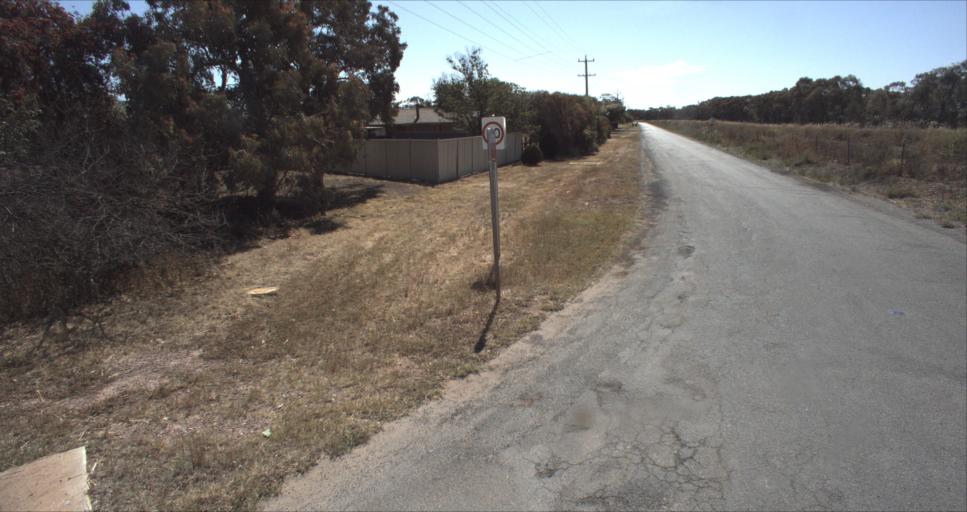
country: AU
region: New South Wales
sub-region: Leeton
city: Leeton
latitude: -34.5509
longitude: 146.3829
